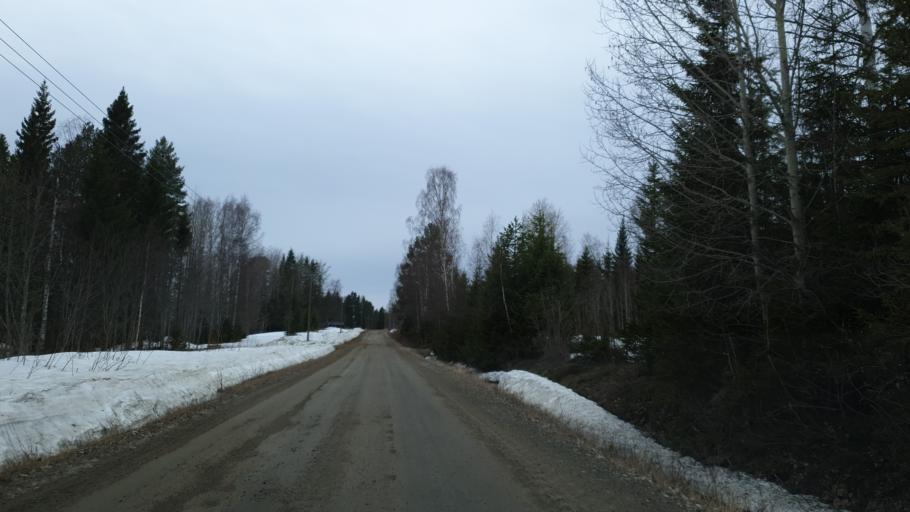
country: SE
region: Vaesterbotten
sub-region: Robertsfors Kommun
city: Robertsfors
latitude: 64.3912
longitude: 20.9744
